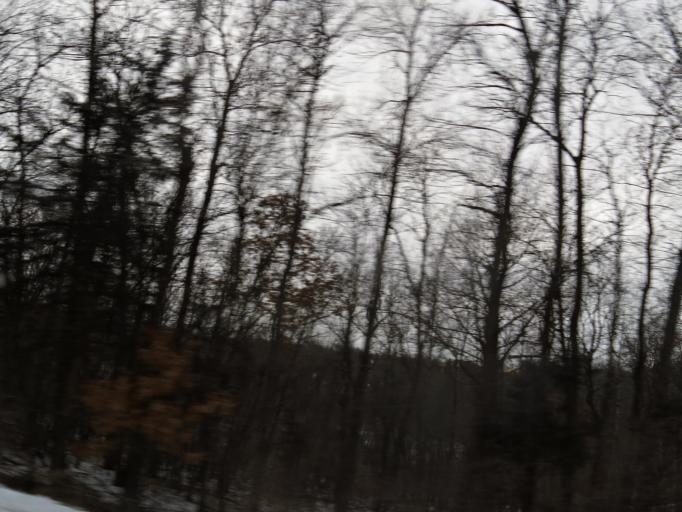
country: US
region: Minnesota
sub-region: Carver County
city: Carver
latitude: 44.7419
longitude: -93.6521
